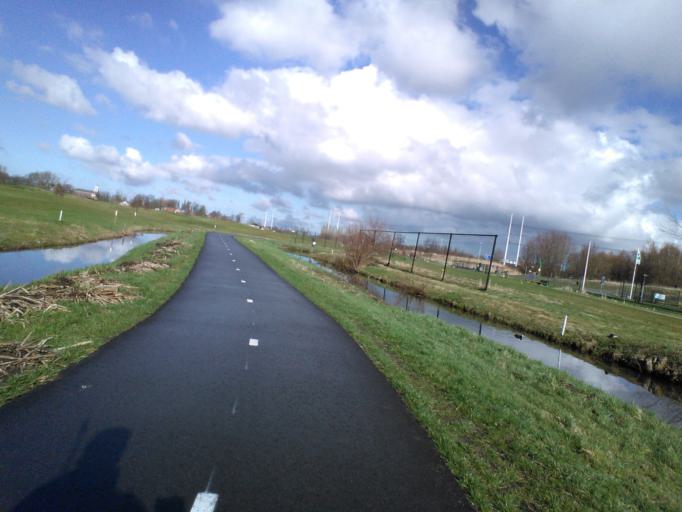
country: NL
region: South Holland
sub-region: Gemeente Delft
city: Delft
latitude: 51.9822
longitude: 4.3257
